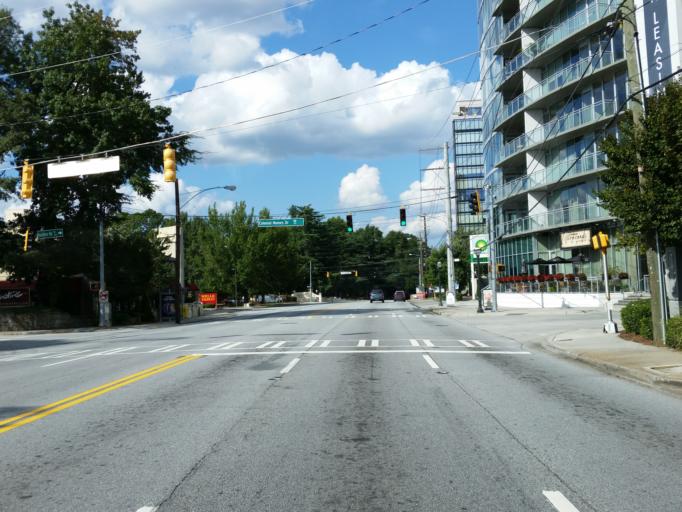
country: US
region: Georgia
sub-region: Fulton County
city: Atlanta
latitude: 33.8134
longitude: -84.3923
